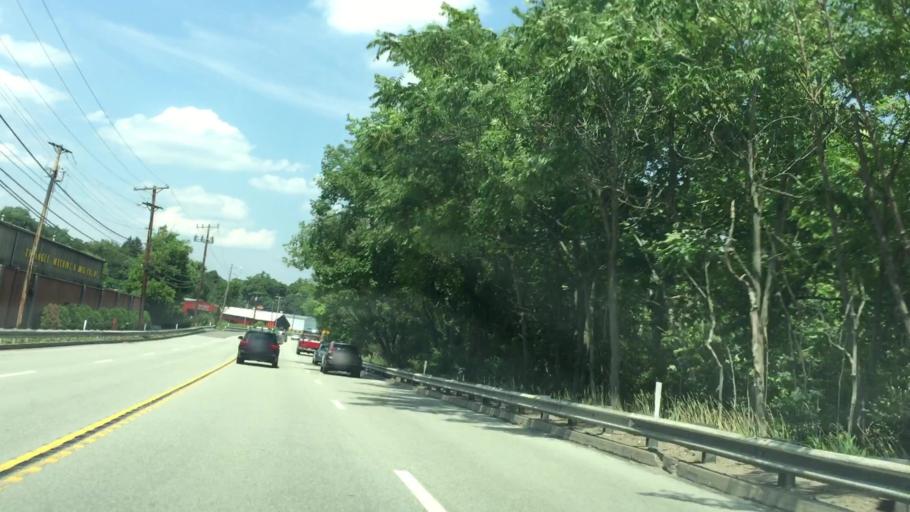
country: US
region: Pennsylvania
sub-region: Allegheny County
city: Etna
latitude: 40.5251
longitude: -79.9479
